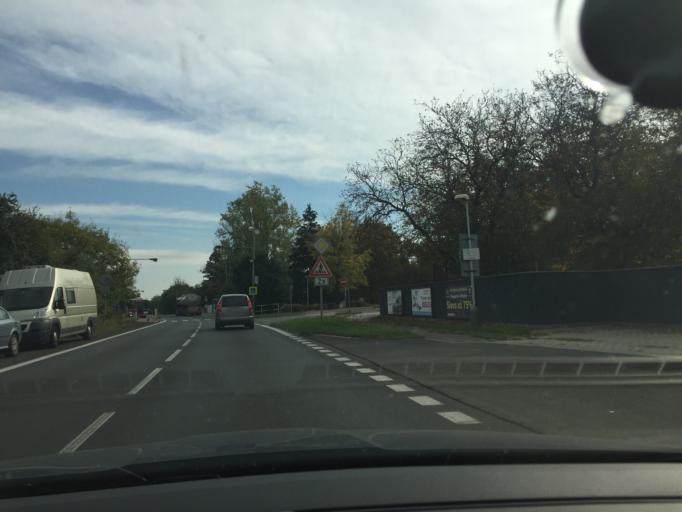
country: CZ
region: Praha
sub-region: Praha 14
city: Hostavice
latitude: 50.0877
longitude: 14.5563
